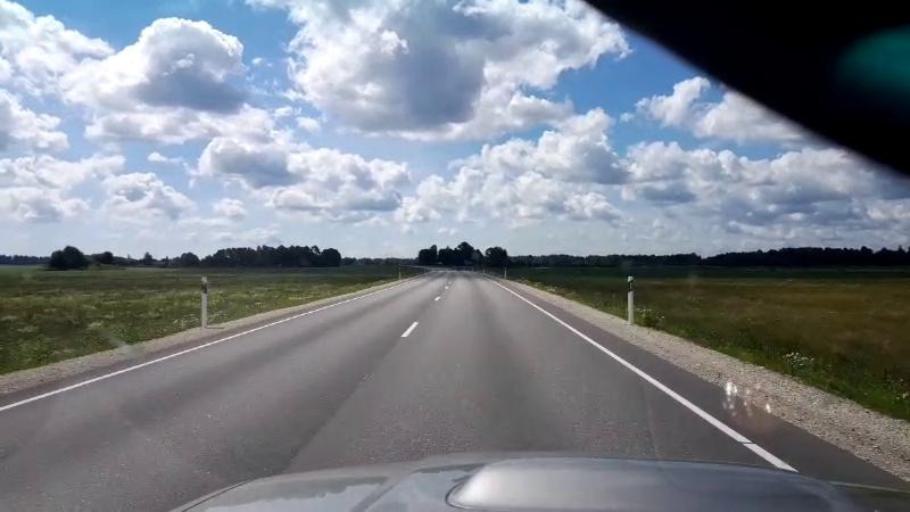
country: EE
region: Jaervamaa
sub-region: Jaerva-Jaani vald
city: Jarva-Jaani
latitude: 59.0874
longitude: 25.6868
